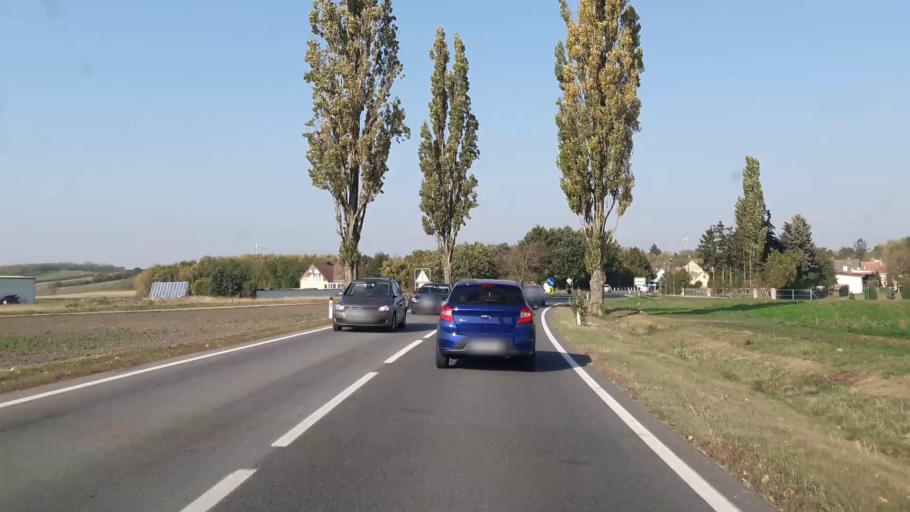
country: AT
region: Lower Austria
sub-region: Politischer Bezirk Ganserndorf
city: Engelhartstetten
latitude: 48.2175
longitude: 16.9000
